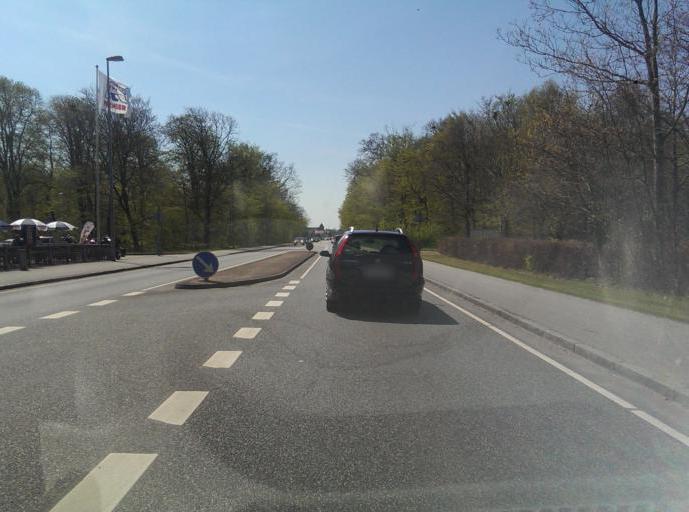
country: DK
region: South Denmark
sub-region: Esbjerg Kommune
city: Ribe
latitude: 55.3407
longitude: 8.7739
